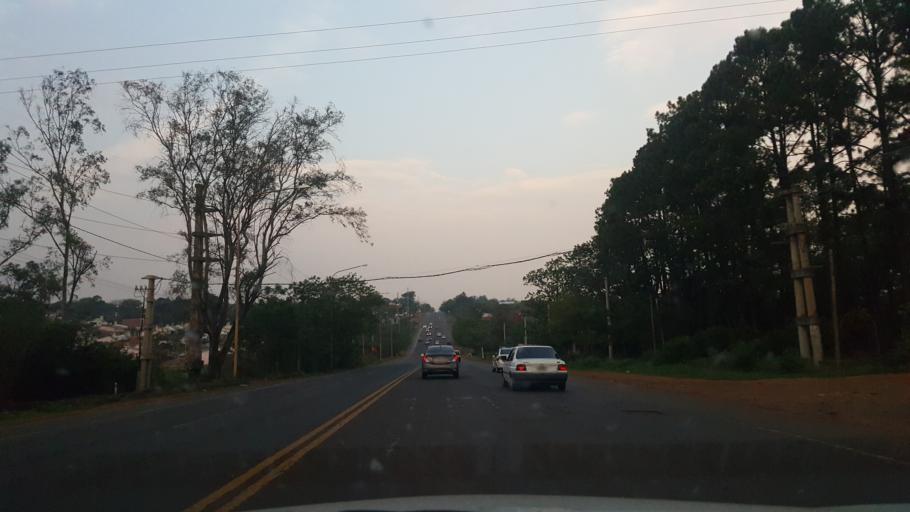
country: AR
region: Misiones
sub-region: Departamento de Capital
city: Posadas
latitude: -27.3994
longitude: -55.9481
